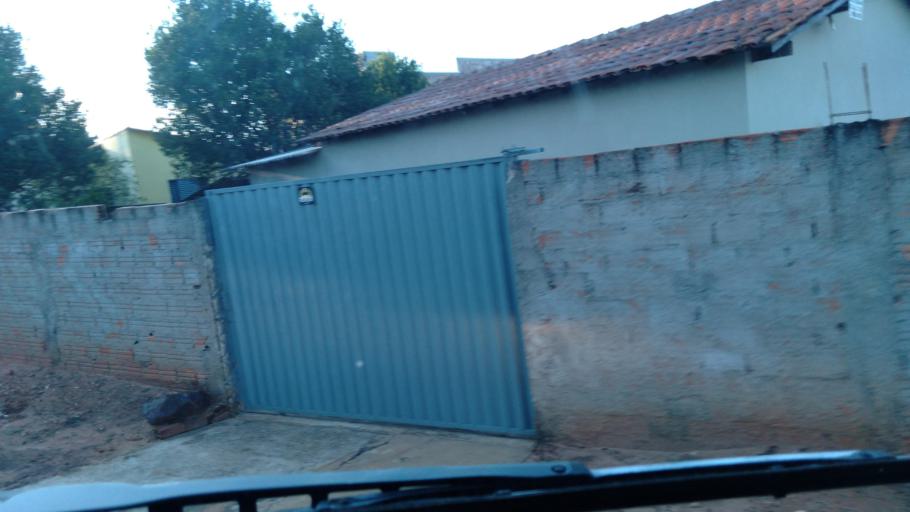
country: BR
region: Goias
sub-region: Mineiros
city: Mineiros
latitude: -17.5726
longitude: -52.5707
